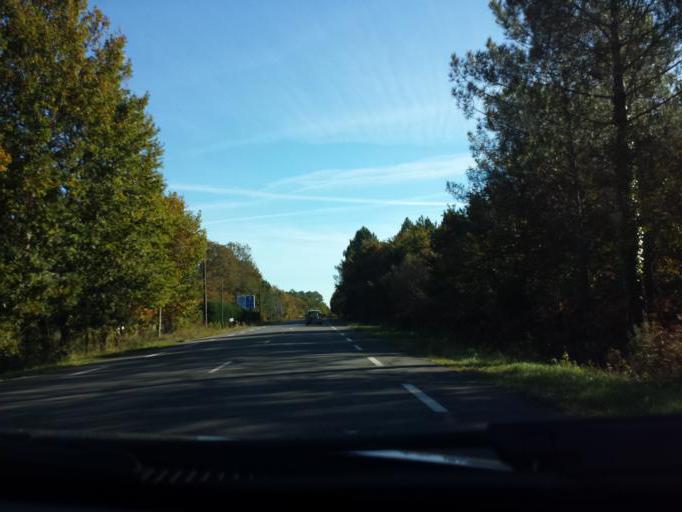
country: FR
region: Aquitaine
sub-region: Departement de la Gironde
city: Lacanau
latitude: 44.9758
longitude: -1.0210
